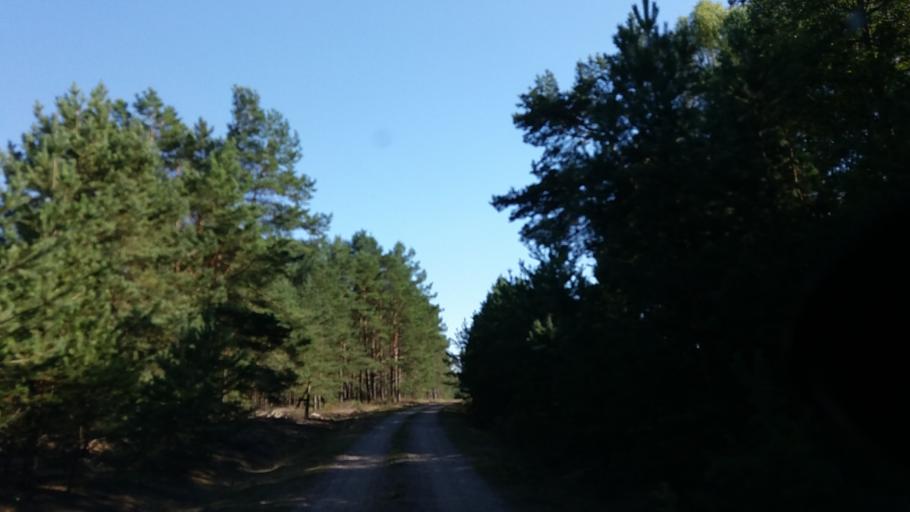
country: PL
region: West Pomeranian Voivodeship
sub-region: Powiat szczecinecki
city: Borne Sulinowo
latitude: 53.5623
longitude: 16.5025
